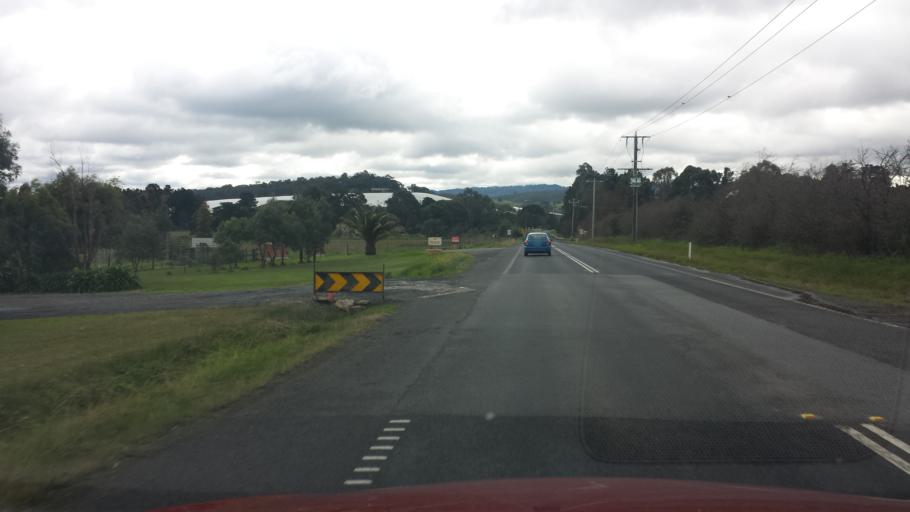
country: AU
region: Victoria
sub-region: Casey
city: Narre Warren North
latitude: -37.9754
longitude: 145.3152
